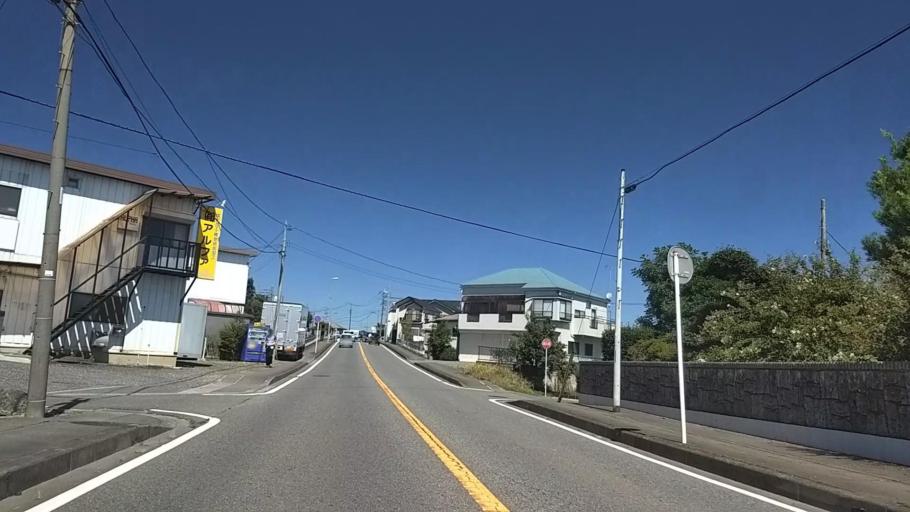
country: JP
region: Tokyo
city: Hachioji
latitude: 35.5773
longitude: 139.3155
